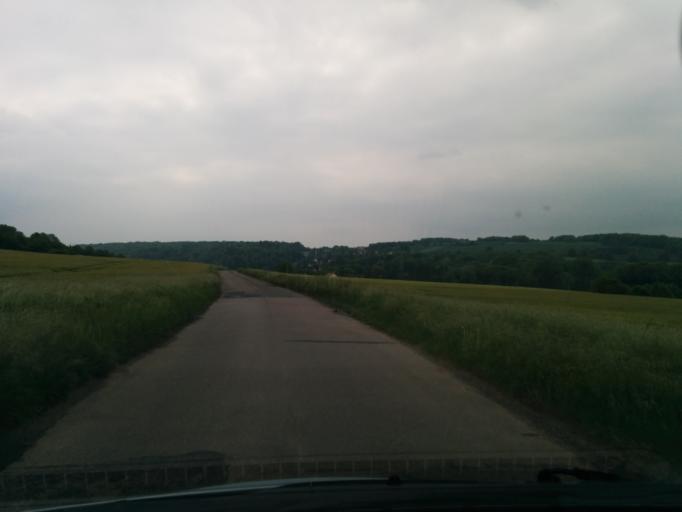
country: FR
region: Ile-de-France
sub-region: Departement des Yvelines
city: Epone
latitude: 48.9543
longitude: 1.8372
